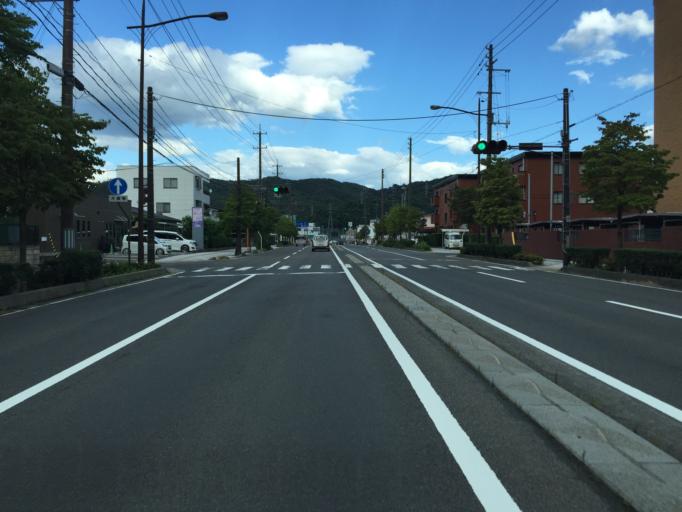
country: JP
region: Fukushima
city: Fukushima-shi
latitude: 37.7564
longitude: 140.4782
